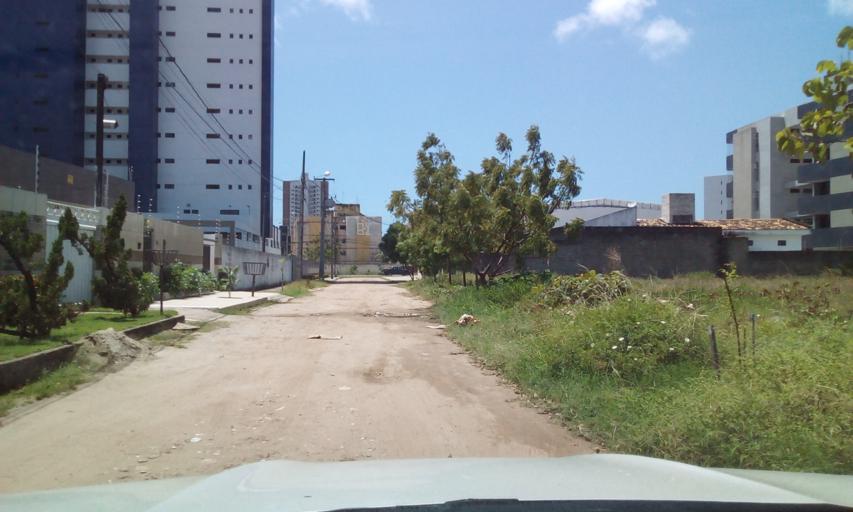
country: BR
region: Paraiba
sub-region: Joao Pessoa
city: Joao Pessoa
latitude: -7.0781
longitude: -34.8413
